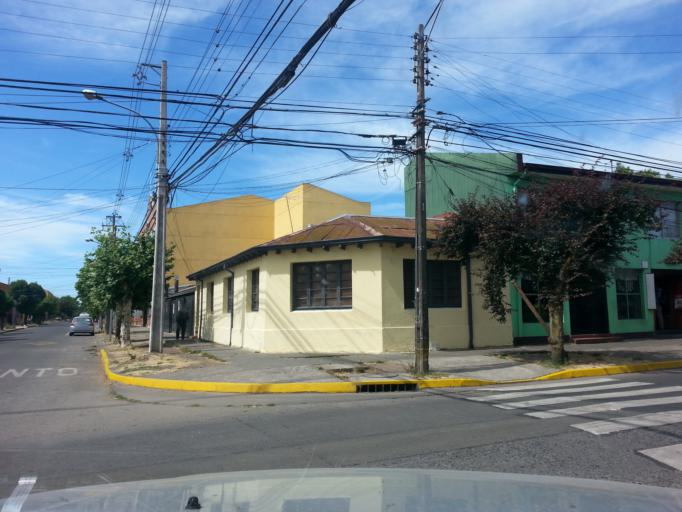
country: CL
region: Biobio
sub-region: Provincia de Nuble
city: Chillan
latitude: -36.6057
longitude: -72.0938
